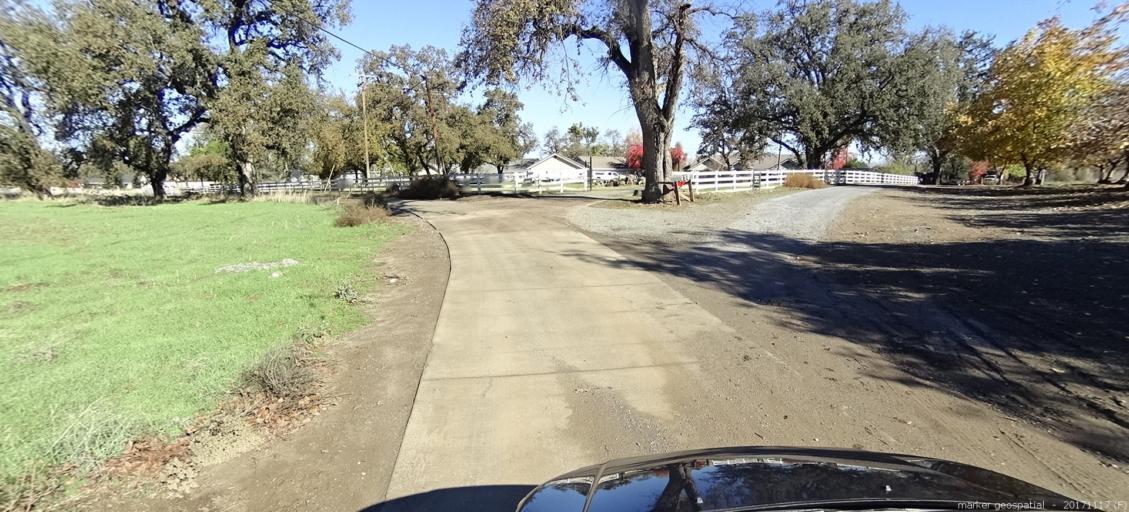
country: US
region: California
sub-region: Shasta County
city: Cottonwood
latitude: 40.4317
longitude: -122.2039
